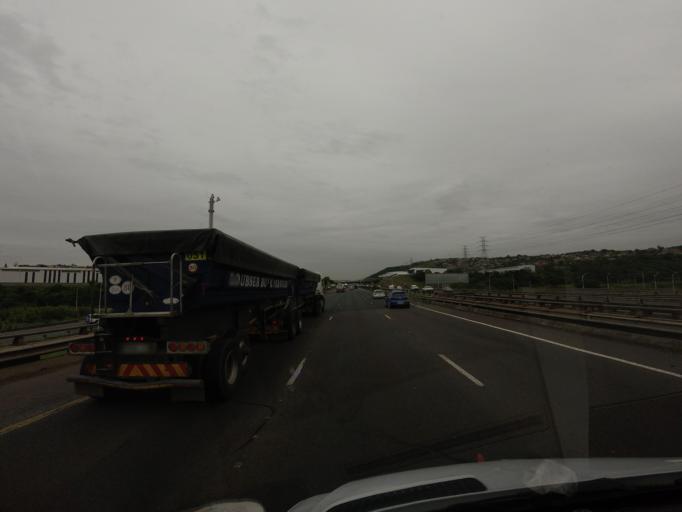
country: ZA
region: KwaZulu-Natal
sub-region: eThekwini Metropolitan Municipality
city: Berea
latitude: -29.7569
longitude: 31.0170
